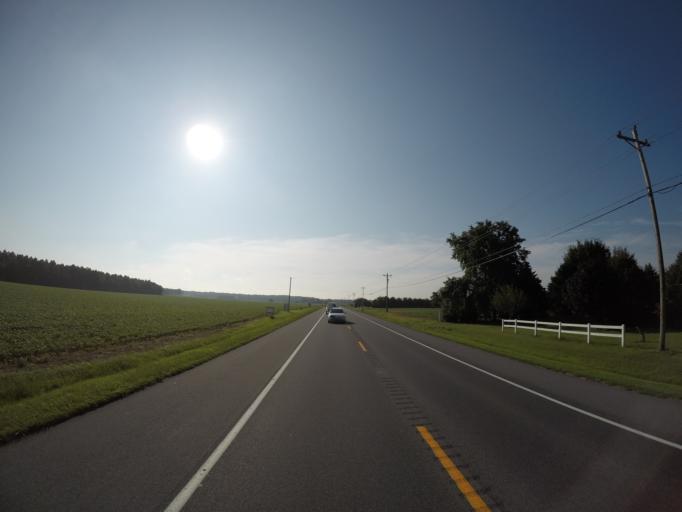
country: US
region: Delaware
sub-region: Sussex County
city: Georgetown
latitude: 38.6982
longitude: -75.4954
